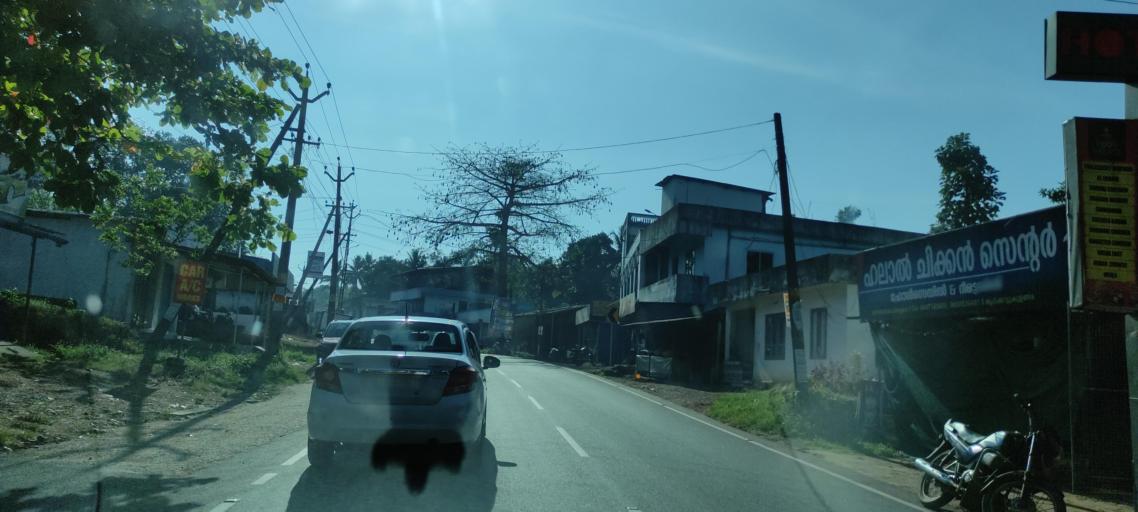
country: IN
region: Kerala
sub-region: Pattanamtitta
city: Adur
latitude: 9.1676
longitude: 76.6627
